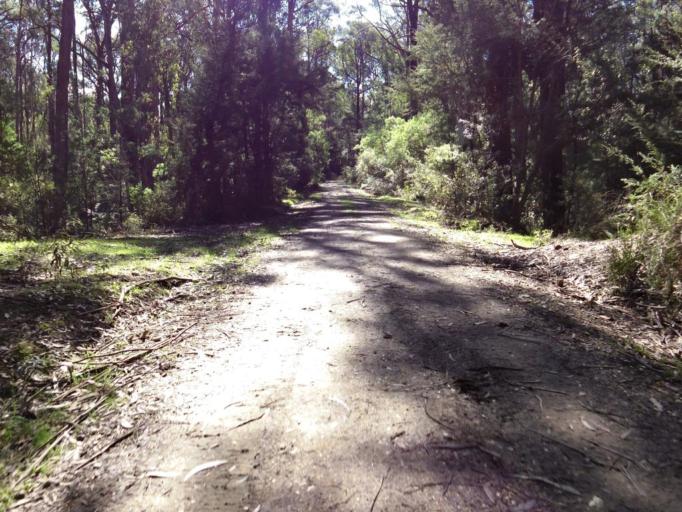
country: AU
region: Victoria
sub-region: Baw Baw
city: Warragul
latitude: -38.0593
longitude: 145.9485
